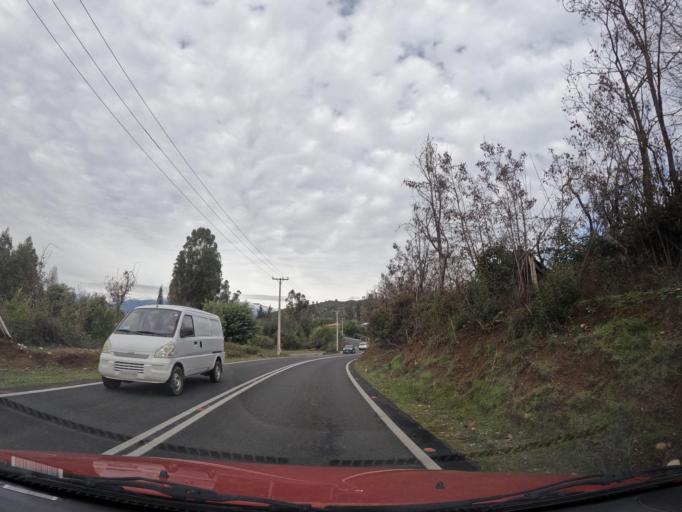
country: CL
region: Maule
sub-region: Provincia de Linares
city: Linares
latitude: -35.9181
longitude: -71.4622
